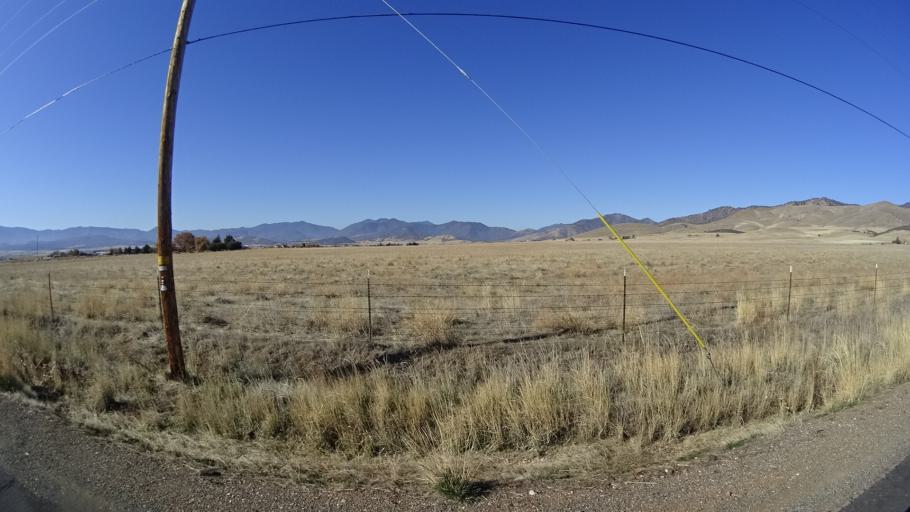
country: US
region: California
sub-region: Siskiyou County
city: Montague
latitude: 41.7636
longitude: -122.5230
